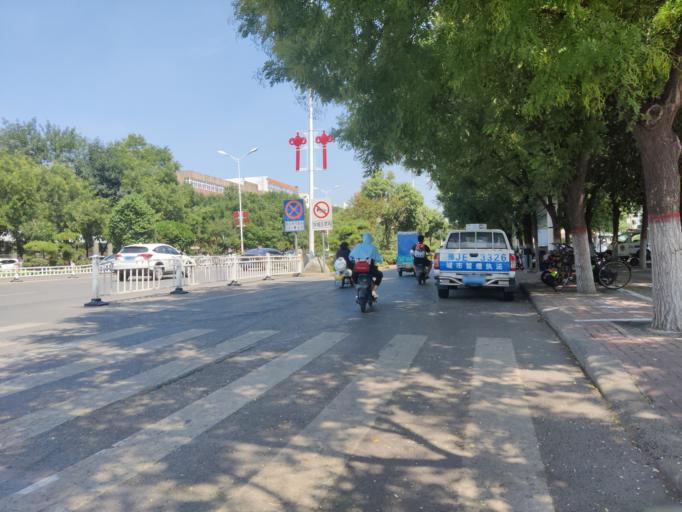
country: CN
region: Henan Sheng
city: Puyang
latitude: 35.7731
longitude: 115.0203
